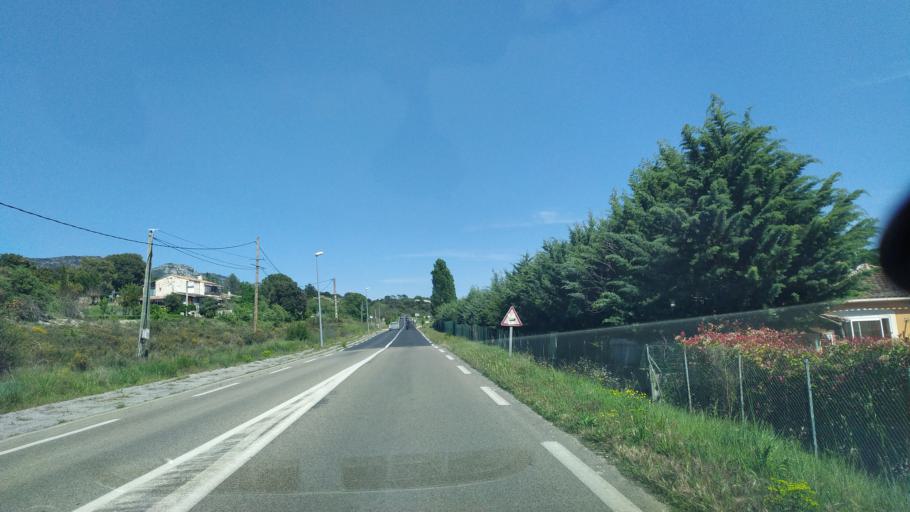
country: FR
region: Languedoc-Roussillon
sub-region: Departement de l'Herault
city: Laroque
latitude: 43.9450
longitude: 3.7360
